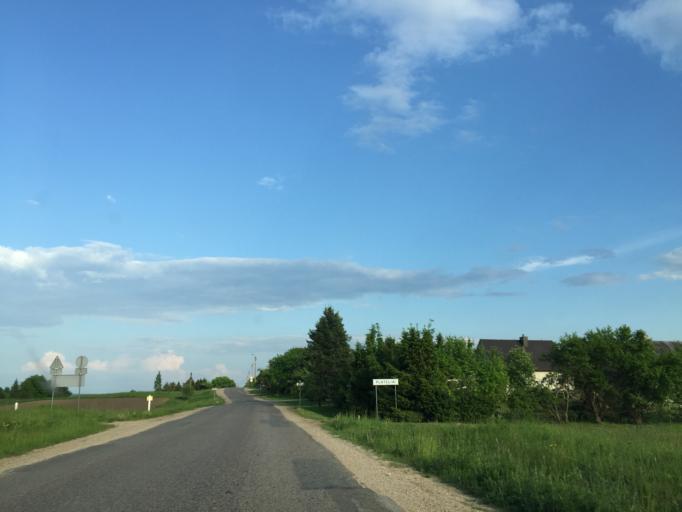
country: LT
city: Plateliai
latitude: 56.0456
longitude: 21.8057
